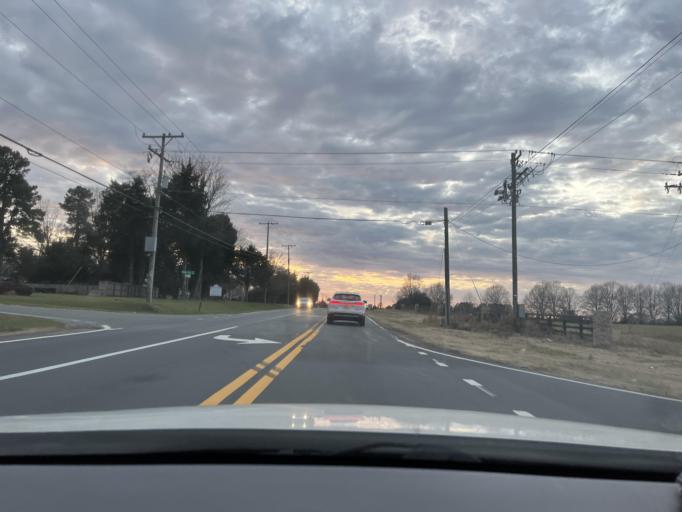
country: US
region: North Carolina
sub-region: Guilford County
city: Gibsonville
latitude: 36.0709
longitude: -79.5823
